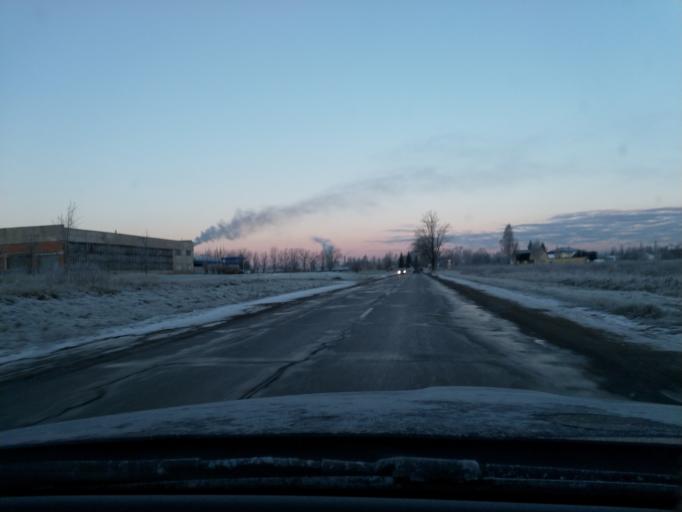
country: LV
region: Kuldigas Rajons
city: Kuldiga
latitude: 56.9545
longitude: 21.9915
